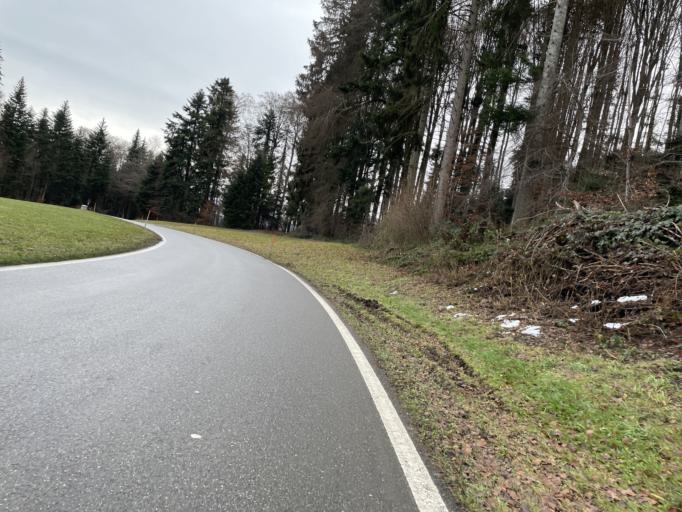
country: CH
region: Bern
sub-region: Bern-Mittelland District
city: Munsingen
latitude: 46.8528
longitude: 7.5438
